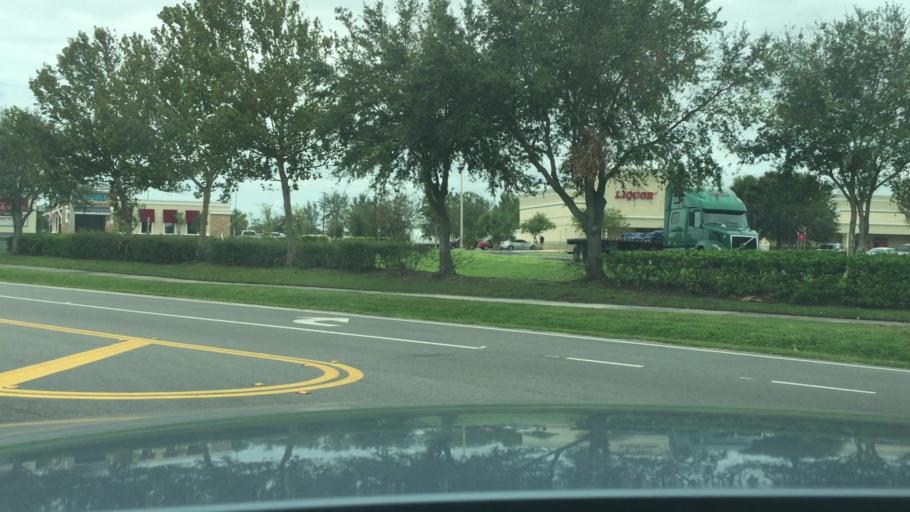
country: US
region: Florida
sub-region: Osceola County
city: Saint Cloud
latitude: 28.1980
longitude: -81.2947
